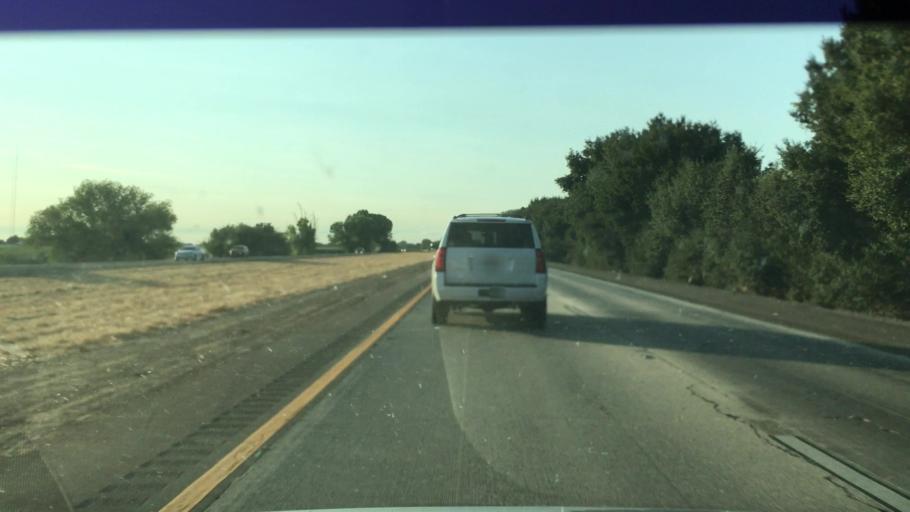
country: US
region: California
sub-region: San Joaquin County
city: Thornton
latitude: 38.2364
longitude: -121.4380
